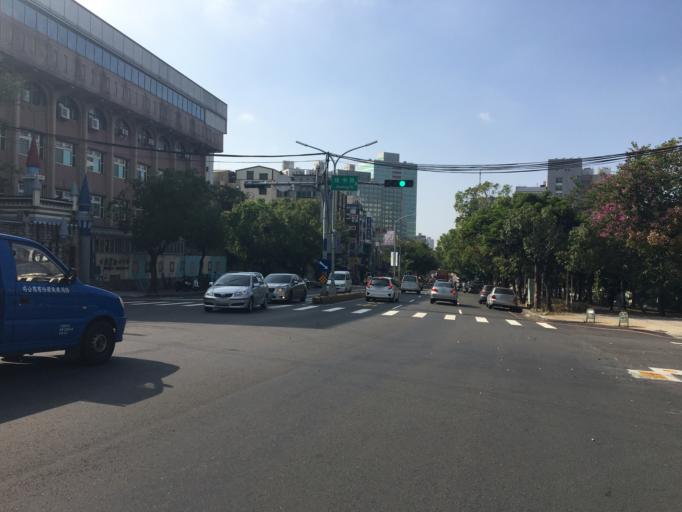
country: TW
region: Taiwan
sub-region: Hsinchu
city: Hsinchu
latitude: 24.7989
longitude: 120.9937
